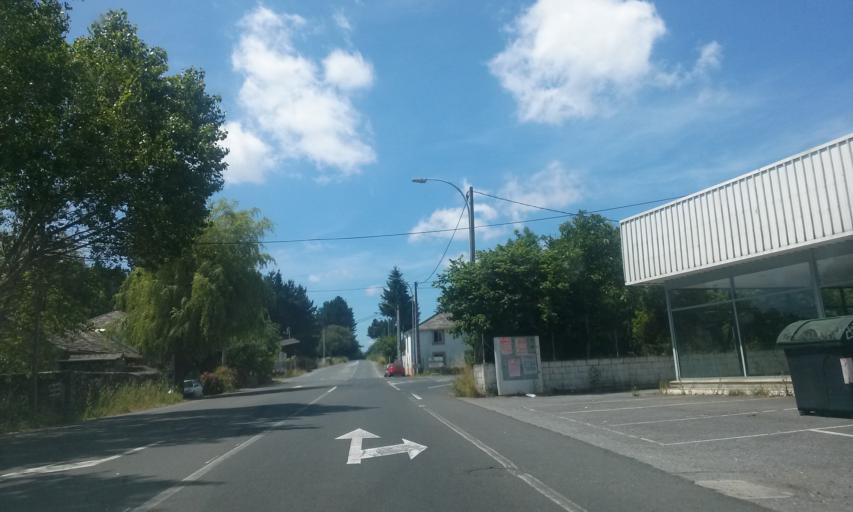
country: ES
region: Galicia
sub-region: Provincia de Lugo
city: Lugo
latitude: 42.9892
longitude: -7.5790
